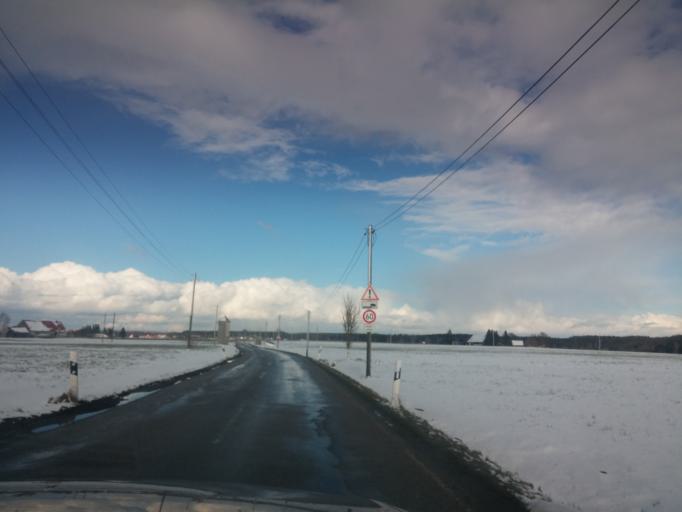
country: DE
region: Bavaria
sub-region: Swabia
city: Kronburg
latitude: 47.9340
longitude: 10.1535
